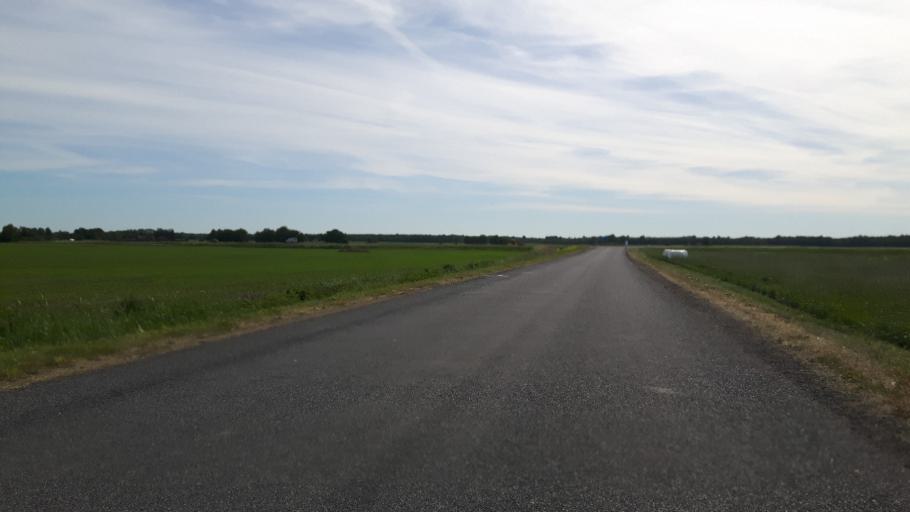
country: EE
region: Harju
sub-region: Raasiku vald
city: Arukula
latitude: 59.4219
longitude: 25.0800
